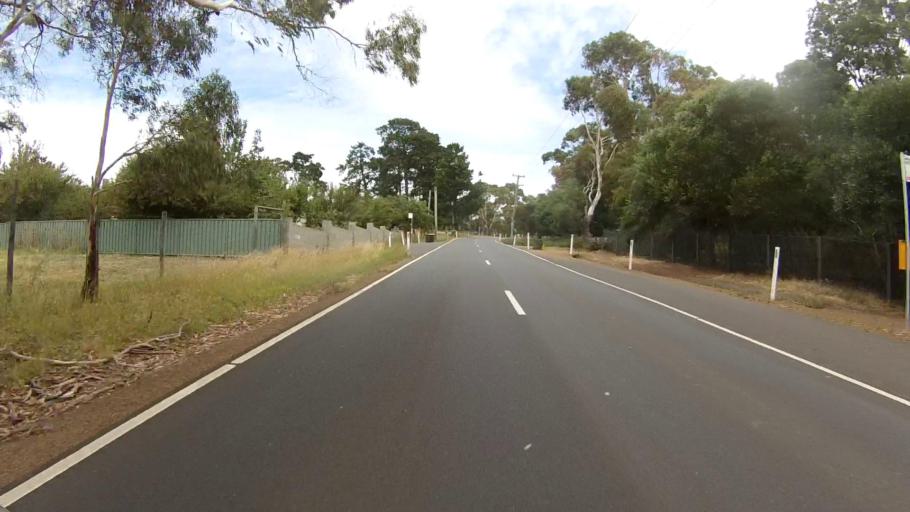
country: AU
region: Tasmania
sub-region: Clarence
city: Acton Park
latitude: -42.8666
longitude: 147.4881
